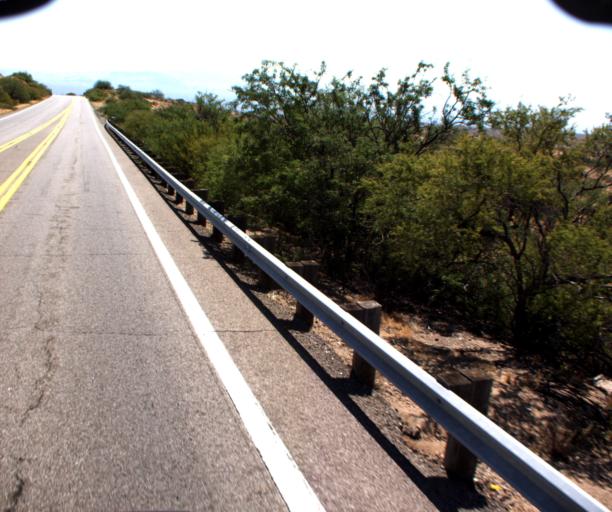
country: US
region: Arizona
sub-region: Pinal County
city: Oracle
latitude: 32.6471
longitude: -110.7172
